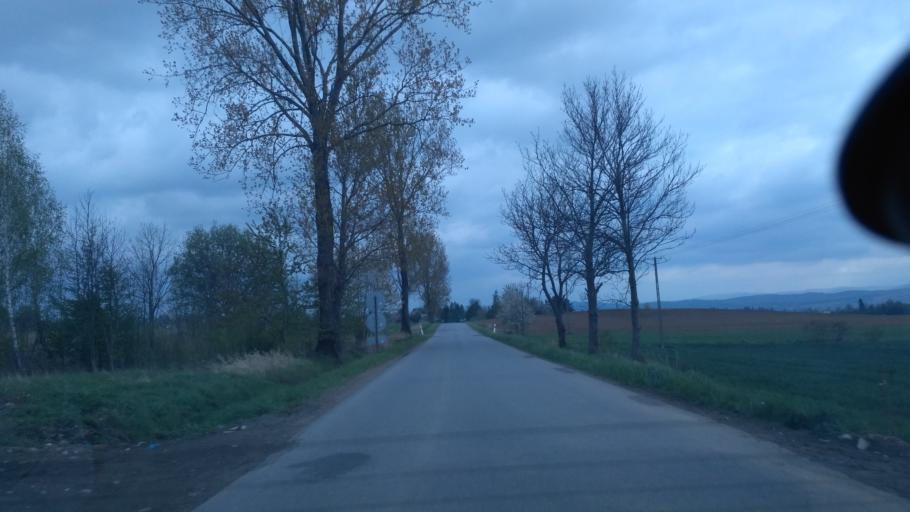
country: PL
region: Subcarpathian Voivodeship
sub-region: Powiat brzozowski
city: Turze Pole
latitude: 49.6312
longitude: 22.0076
